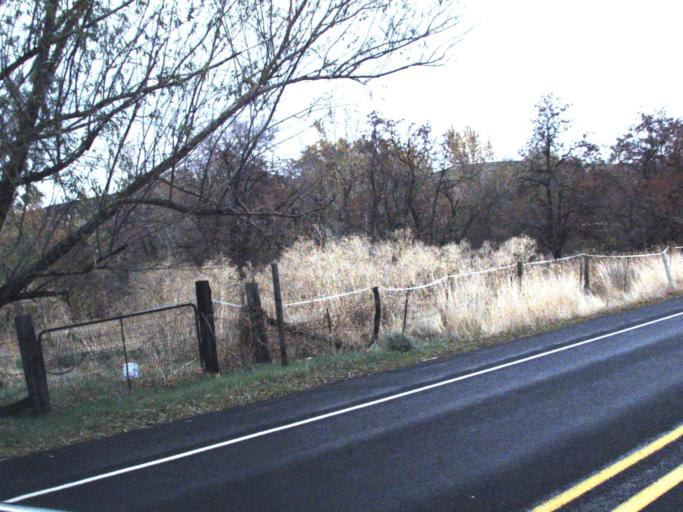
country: US
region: Washington
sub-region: Walla Walla County
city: Waitsburg
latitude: 46.1388
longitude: -118.1587
